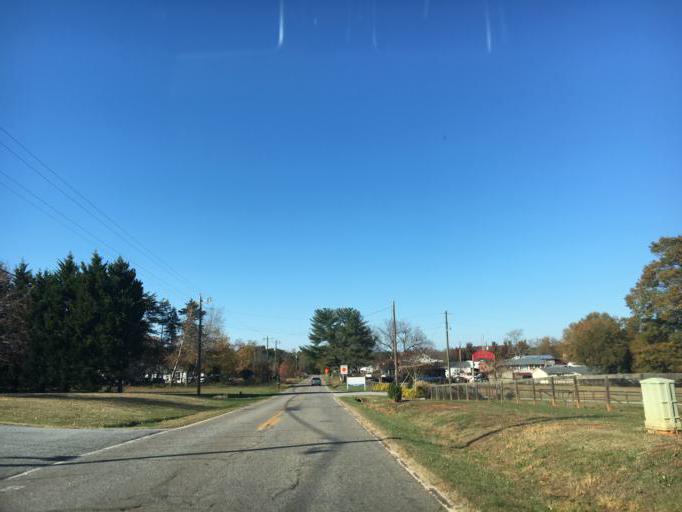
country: US
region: South Carolina
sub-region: Spartanburg County
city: Wellford
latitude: 34.9799
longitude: -82.0753
